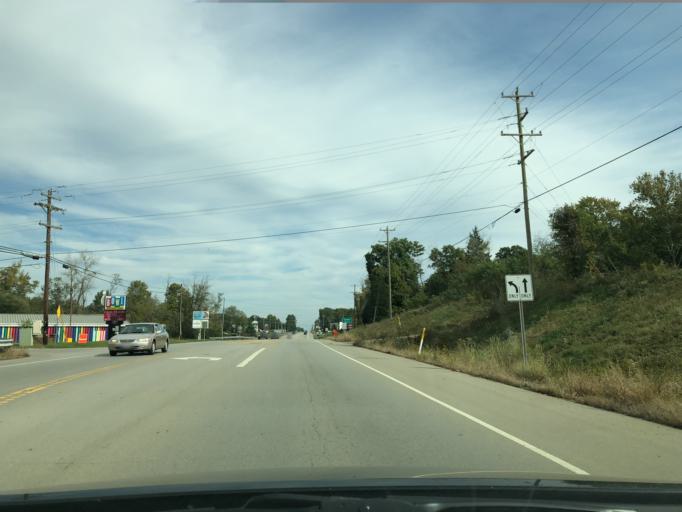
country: US
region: Ohio
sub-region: Clermont County
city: Mount Repose
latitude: 39.2085
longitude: -84.2118
